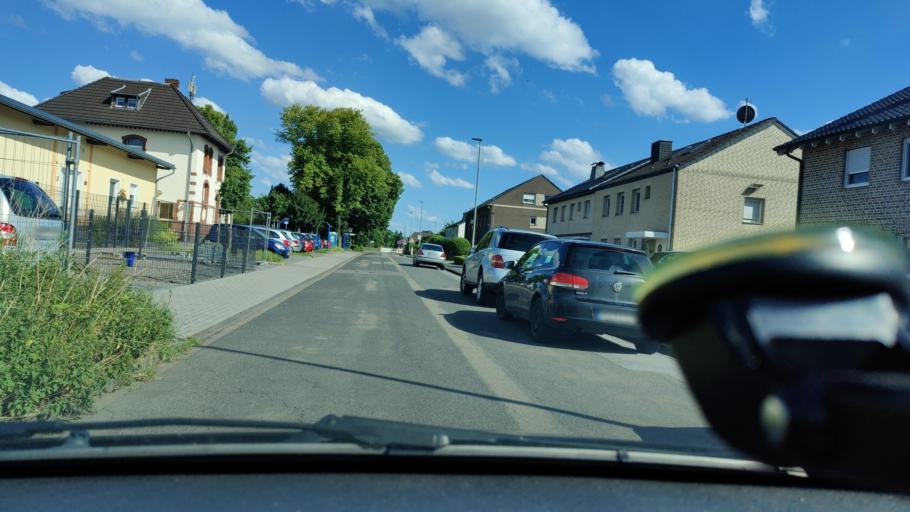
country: DE
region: North Rhine-Westphalia
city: Rheinberg
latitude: 51.5601
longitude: 6.5559
